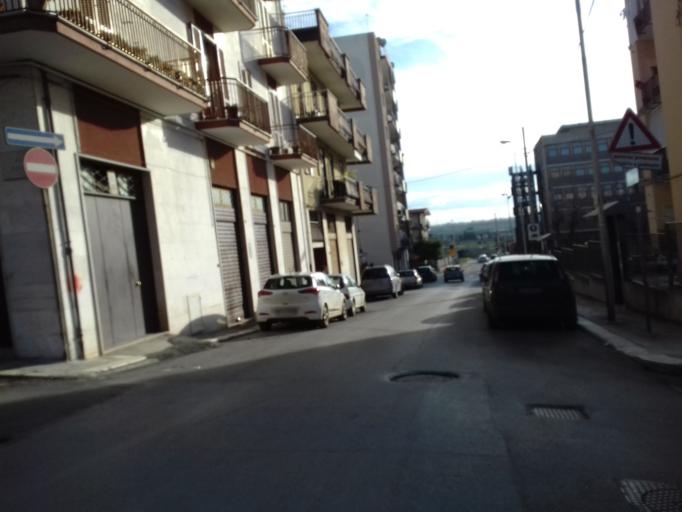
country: IT
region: Apulia
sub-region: Provincia di Bari
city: Ruvo di Puglia
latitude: 41.1149
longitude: 16.4817
